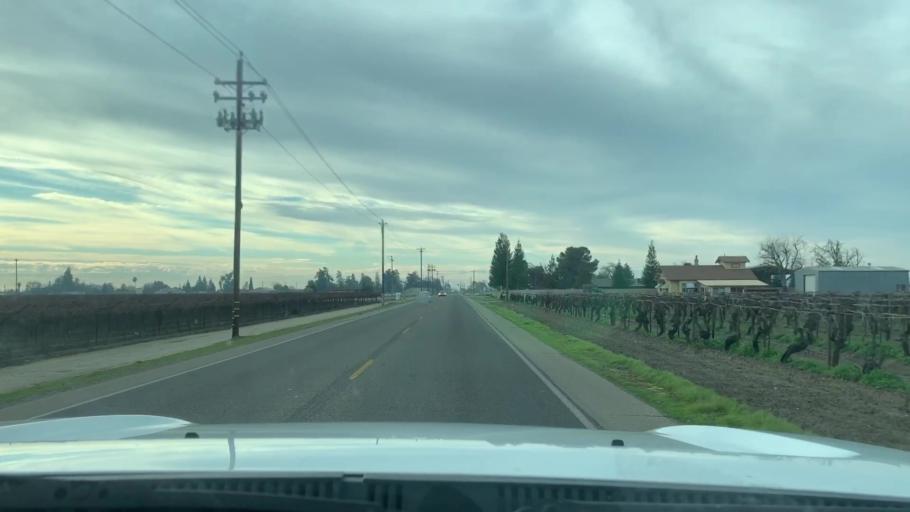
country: US
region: California
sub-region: Fresno County
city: Easton
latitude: 36.6054
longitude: -119.7436
